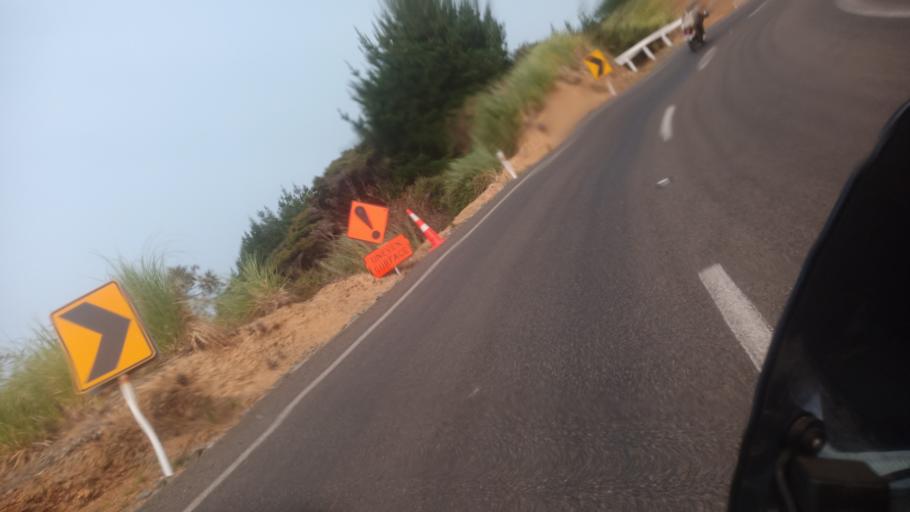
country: NZ
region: Bay of Plenty
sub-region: Opotiki District
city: Opotiki
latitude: -37.8894
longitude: 177.5576
